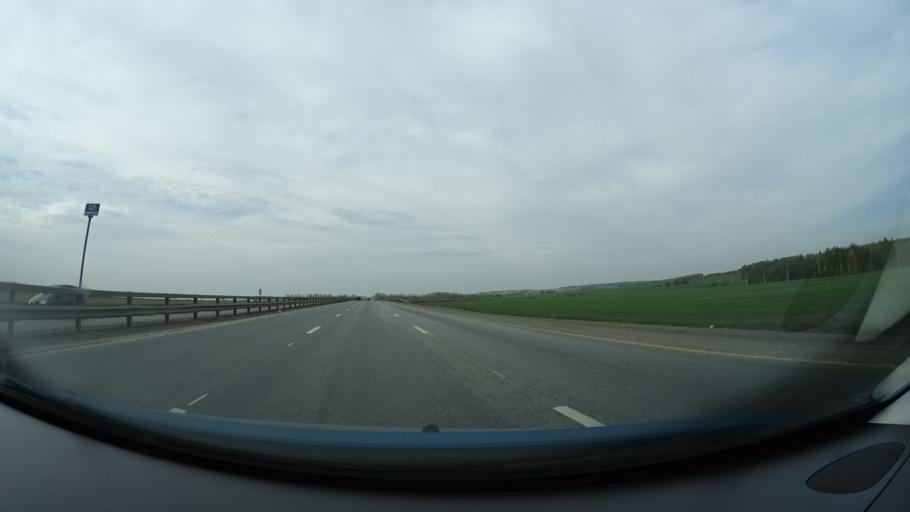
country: RU
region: Bashkortostan
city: Avdon
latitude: 54.6727
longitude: 55.7774
